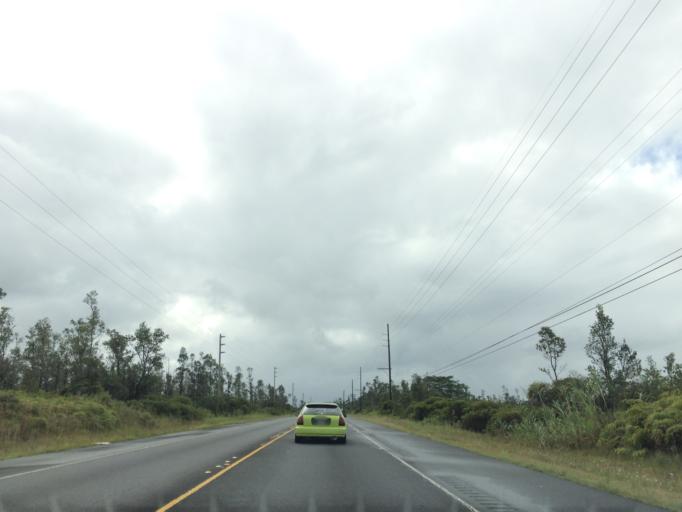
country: US
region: Hawaii
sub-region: Hawaii County
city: Hawaiian Paradise Park
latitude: 19.5173
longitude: -154.9651
